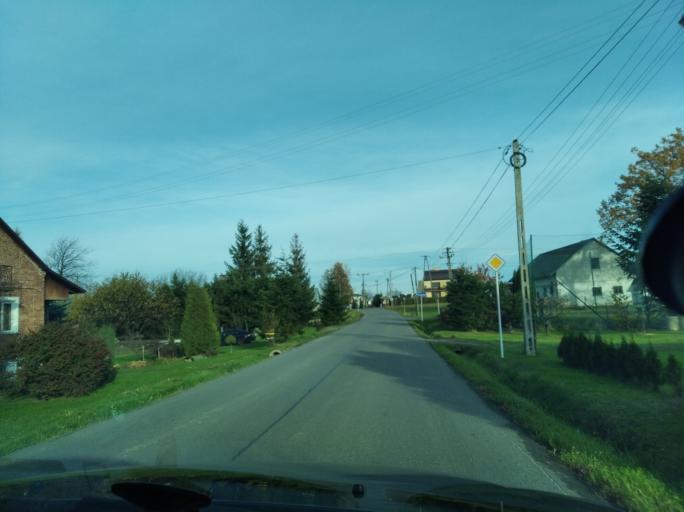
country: PL
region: Subcarpathian Voivodeship
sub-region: Powiat rzeszowski
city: Straszydle
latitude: 49.9370
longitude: 21.9801
